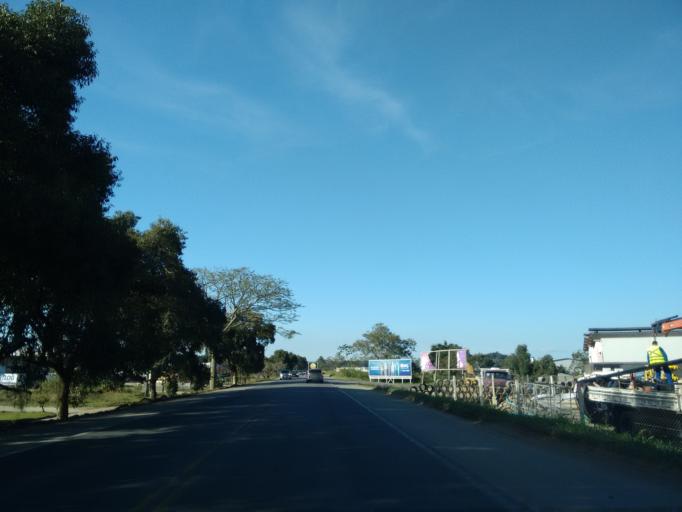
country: BR
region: Santa Catarina
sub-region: Guaramirim
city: Guaramirim
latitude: -26.4709
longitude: -48.9702
